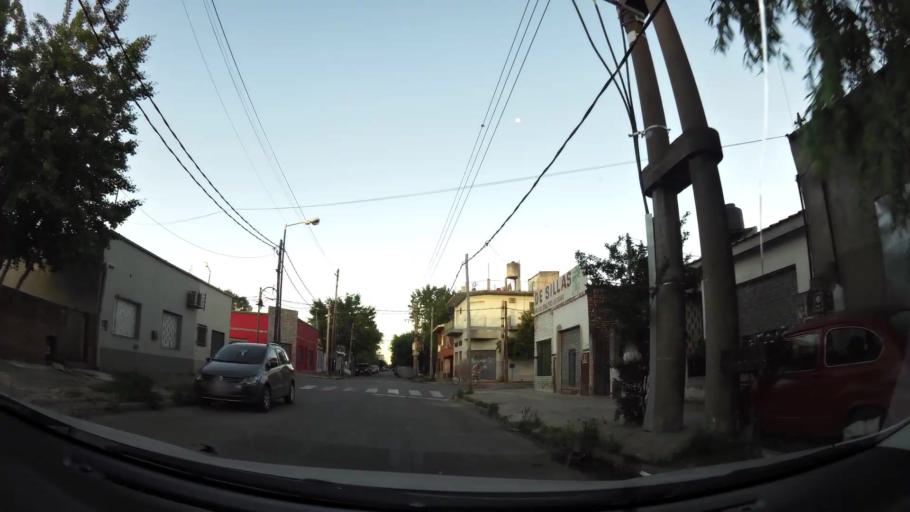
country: AR
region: Buenos Aires
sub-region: Partido de Tigre
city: Tigre
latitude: -34.4443
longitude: -58.5734
